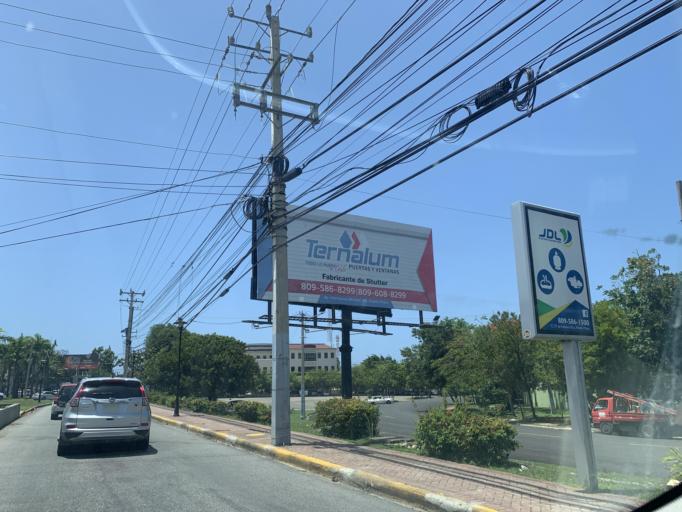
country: DO
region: Puerto Plata
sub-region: Puerto Plata
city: Puerto Plata
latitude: 19.7822
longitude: -70.6724
